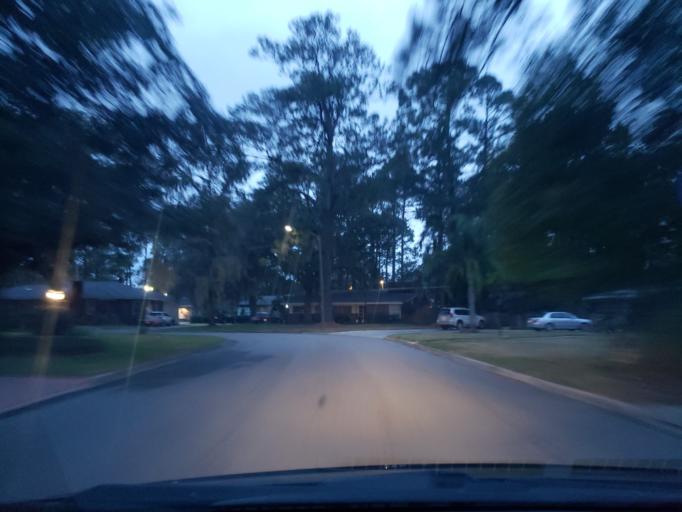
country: US
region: Georgia
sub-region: Chatham County
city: Savannah
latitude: 32.0310
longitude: -81.1055
